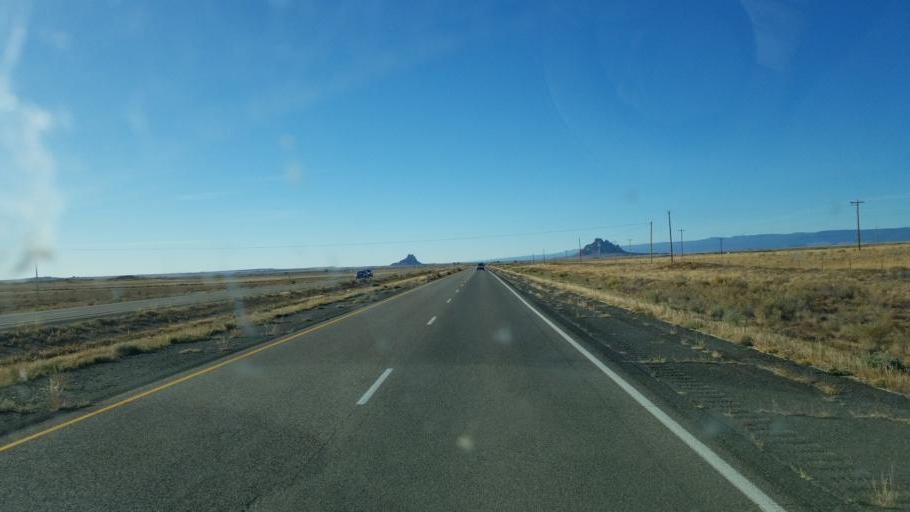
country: US
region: New Mexico
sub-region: San Juan County
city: Shiprock
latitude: 36.4770
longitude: -108.7248
